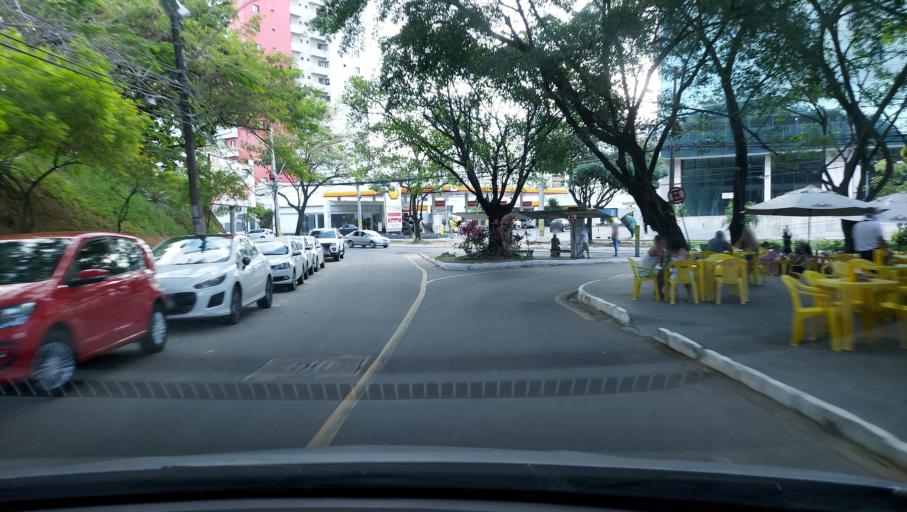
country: BR
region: Bahia
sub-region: Salvador
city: Salvador
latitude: -12.9871
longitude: -38.4480
